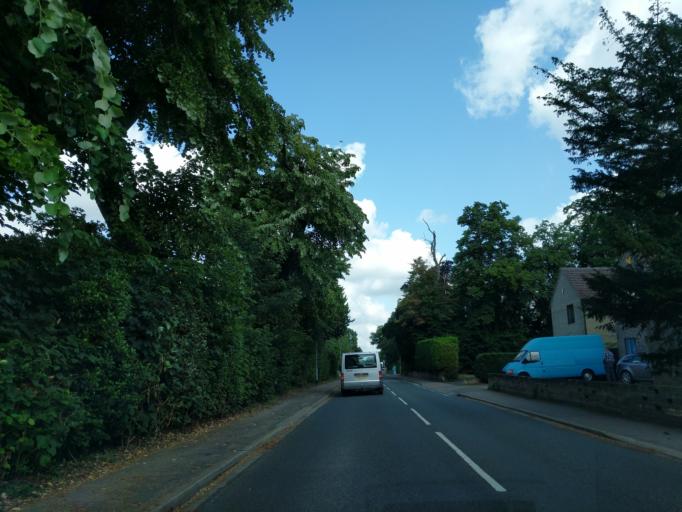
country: GB
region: England
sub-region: Suffolk
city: Exning
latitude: 52.3084
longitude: 0.3835
